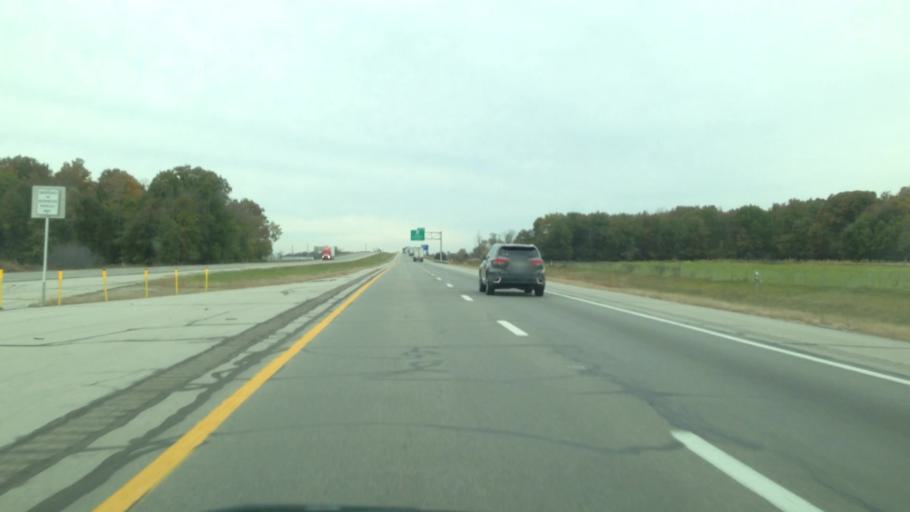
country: US
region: Ohio
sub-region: Williams County
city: Pioneer
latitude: 41.6106
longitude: -84.5228
